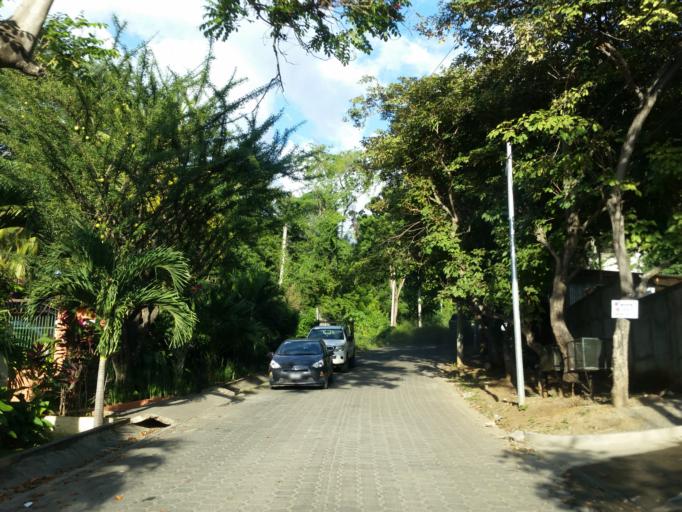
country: NI
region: Managua
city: Managua
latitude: 12.0987
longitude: -86.2380
